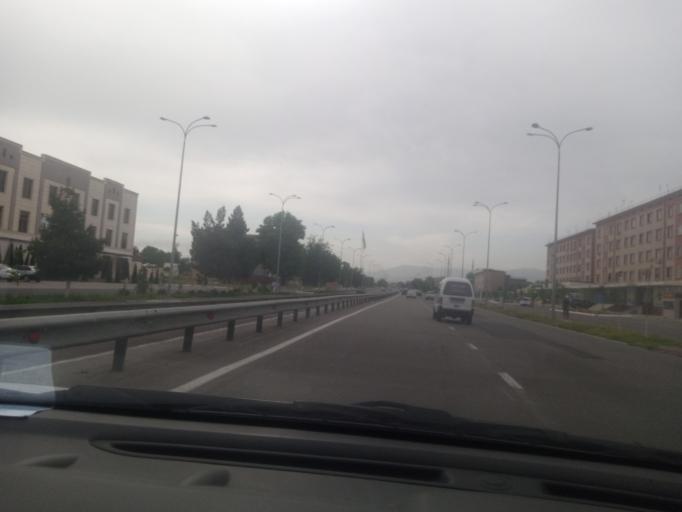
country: UZ
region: Toshkent
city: Ohangaron
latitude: 40.9066
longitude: 69.6315
